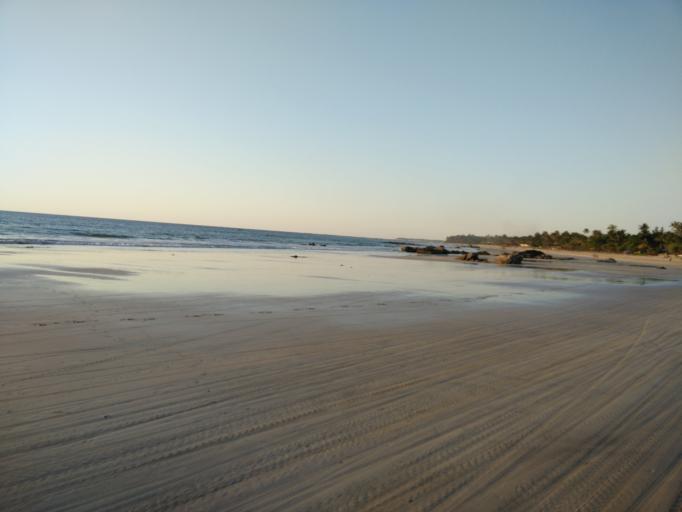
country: MM
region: Ayeyarwady
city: Pathein
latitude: 16.8222
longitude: 94.3967
